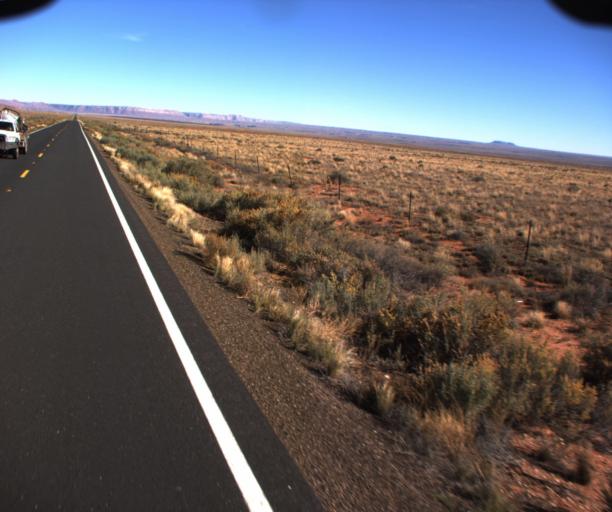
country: US
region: Arizona
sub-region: Coconino County
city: Page
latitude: 36.7068
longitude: -111.9552
